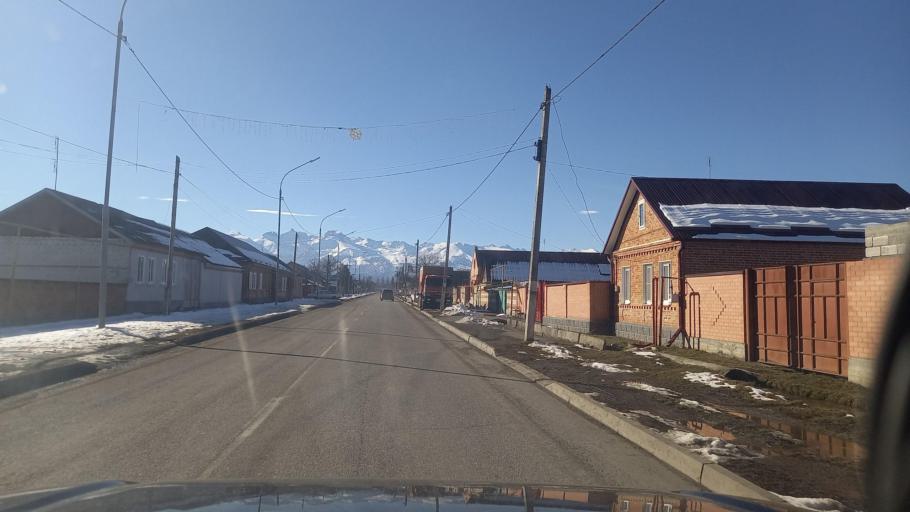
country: RU
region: North Ossetia
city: Chikola
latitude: 43.1934
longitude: 43.9133
